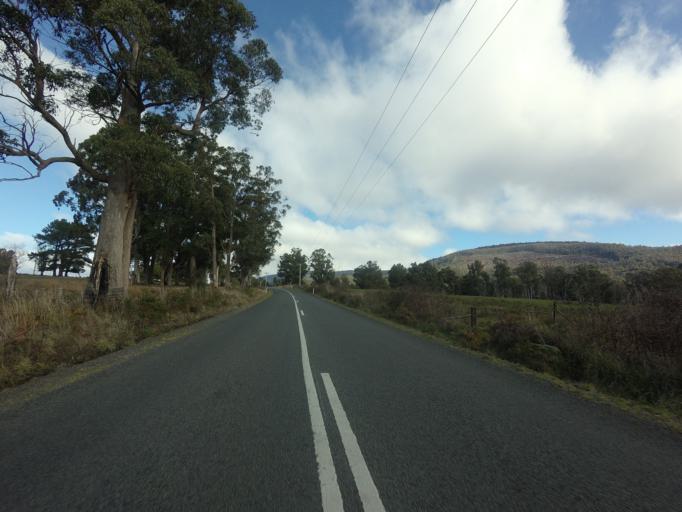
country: AU
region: Tasmania
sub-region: Derwent Valley
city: New Norfolk
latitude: -42.5817
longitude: 146.6948
